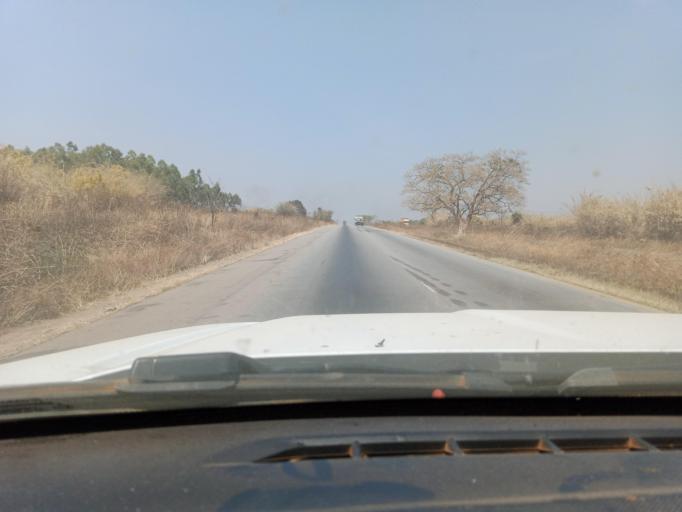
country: ZM
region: Copperbelt
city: Luanshya
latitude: -12.9935
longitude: 28.4180
